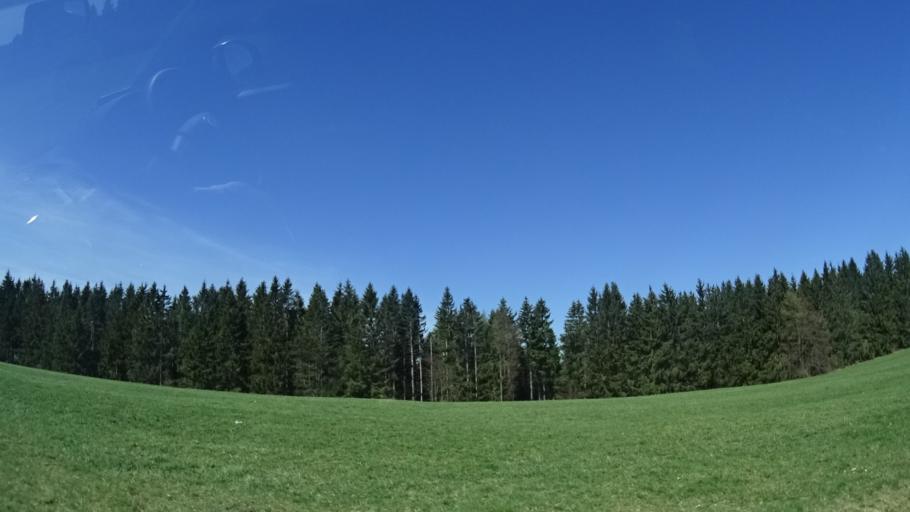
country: DE
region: Thuringia
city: Frauenwald
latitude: 50.5672
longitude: 10.8604
